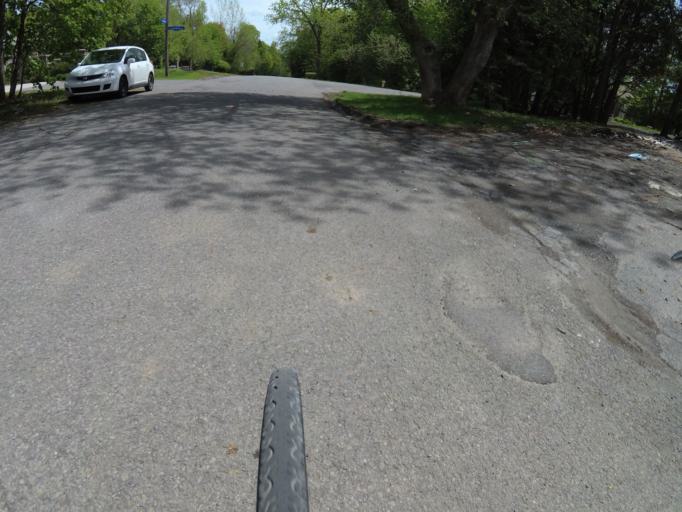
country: CA
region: Quebec
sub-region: Outaouais
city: Gatineau
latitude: 45.4492
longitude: -75.6105
